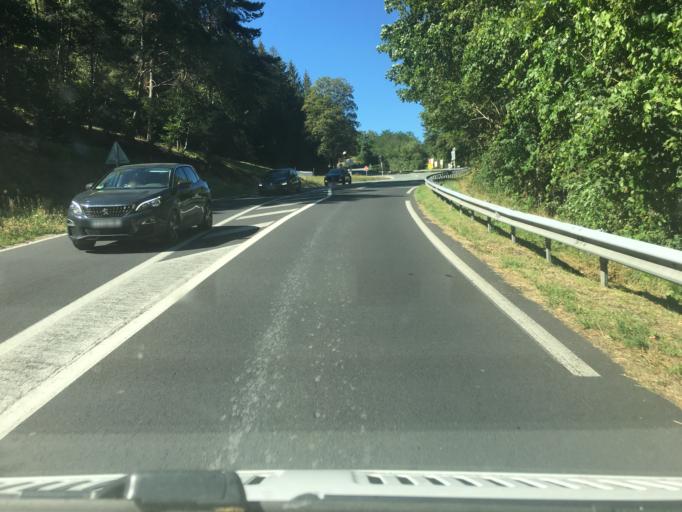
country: FR
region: Limousin
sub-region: Departement de la Correze
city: Bort-les-Orgues
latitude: 45.4166
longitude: 2.5022
